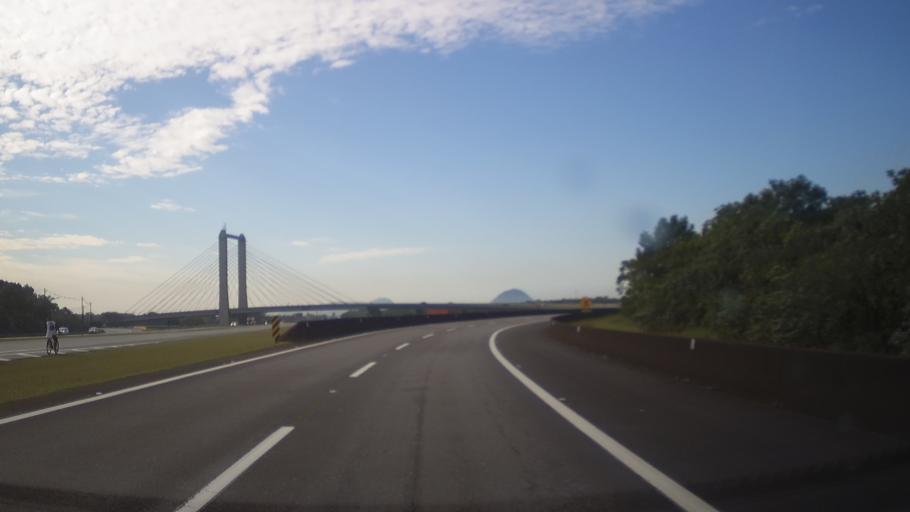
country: BR
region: Sao Paulo
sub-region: Cubatao
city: Cubatao
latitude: -23.9227
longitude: -46.4356
